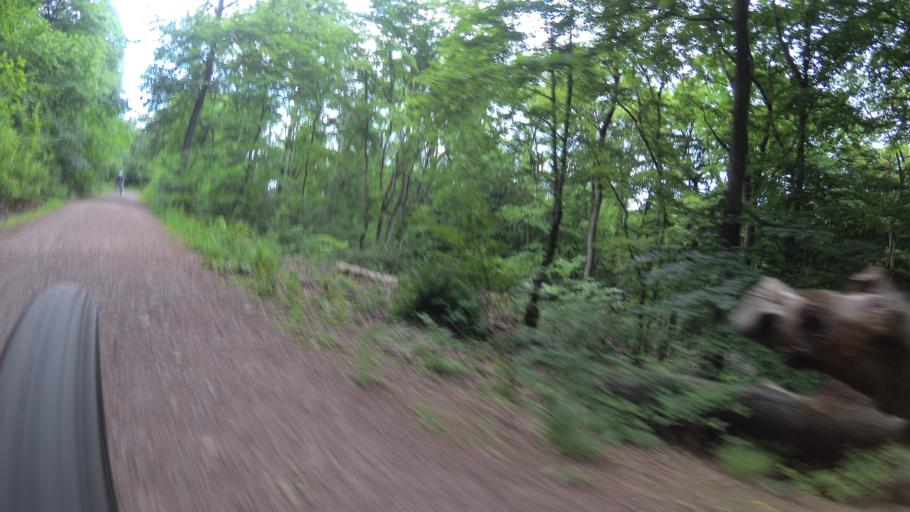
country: DE
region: Saarland
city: Volklingen
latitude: 49.2590
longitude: 6.8780
